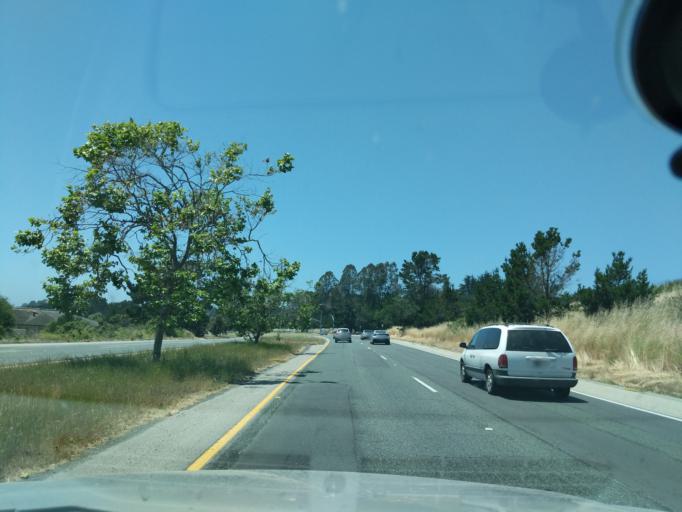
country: US
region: California
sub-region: Monterey County
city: Carmel-by-the-Sea
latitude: 36.5436
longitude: -121.8947
